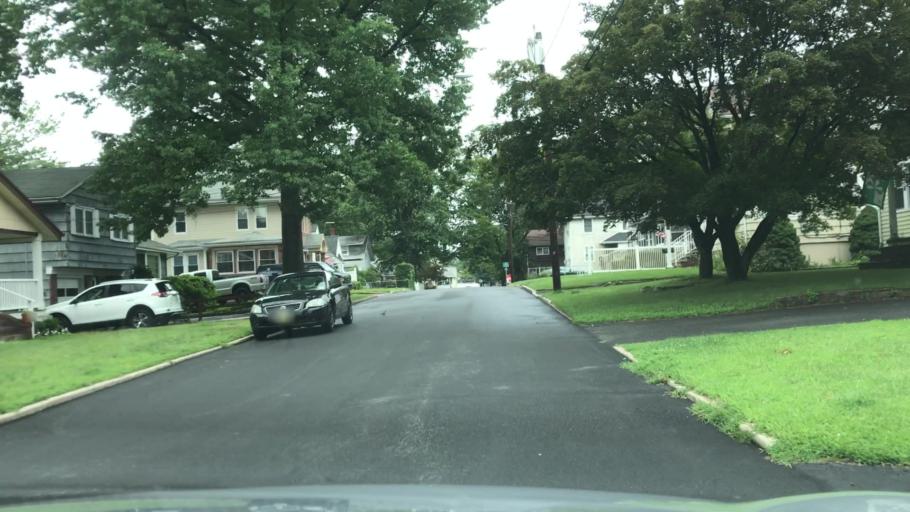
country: US
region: New Jersey
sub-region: Bergen County
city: Bergenfield
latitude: 40.9309
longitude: -73.9852
